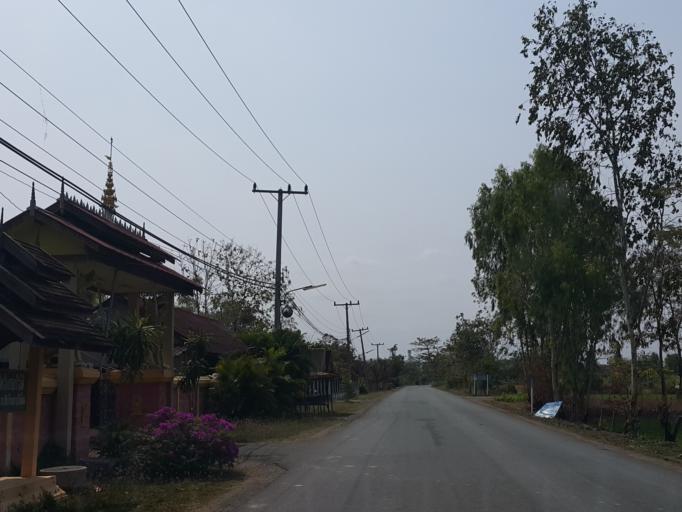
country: TH
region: Lamphun
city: Ban Thi
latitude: 18.6736
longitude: 99.0991
